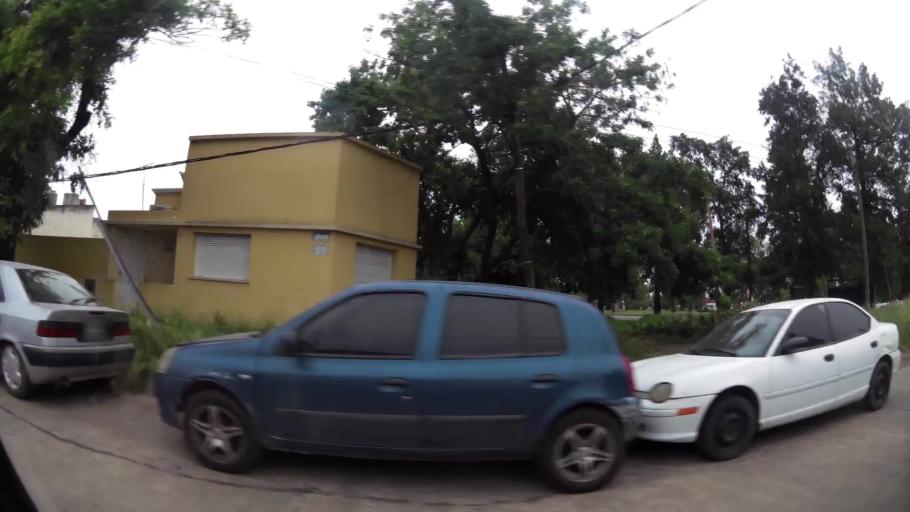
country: AR
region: Buenos Aires
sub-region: Partido de La Plata
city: La Plata
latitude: -34.9197
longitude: -57.9890
